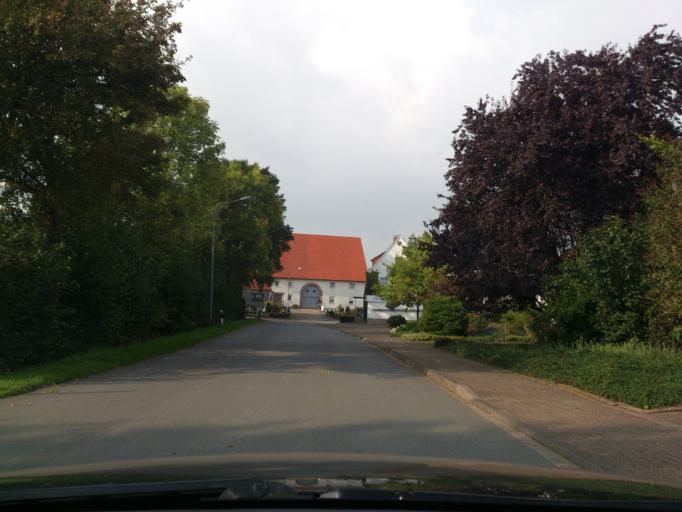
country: DE
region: North Rhine-Westphalia
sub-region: Regierungsbezirk Detmold
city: Willebadessen
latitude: 51.5779
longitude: 9.0376
